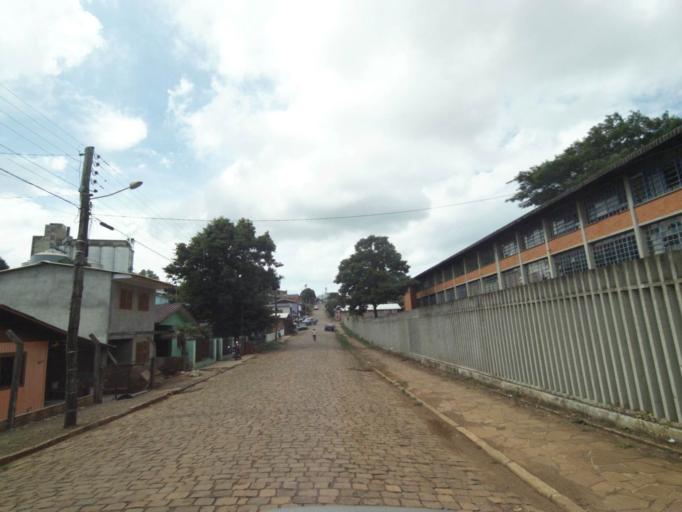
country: BR
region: Rio Grande do Sul
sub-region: Lagoa Vermelha
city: Lagoa Vermelha
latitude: -28.2109
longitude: -51.5400
